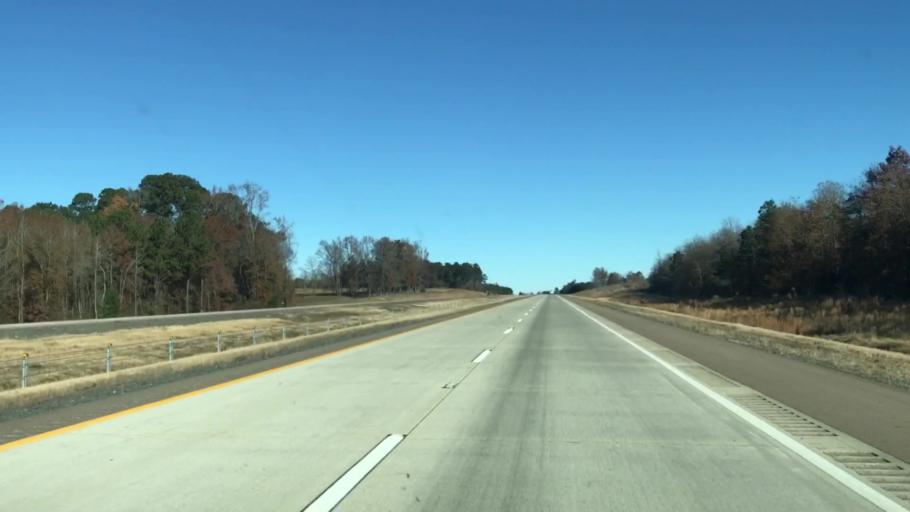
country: US
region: Louisiana
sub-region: Caddo Parish
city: Vivian
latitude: 33.0373
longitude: -93.9007
